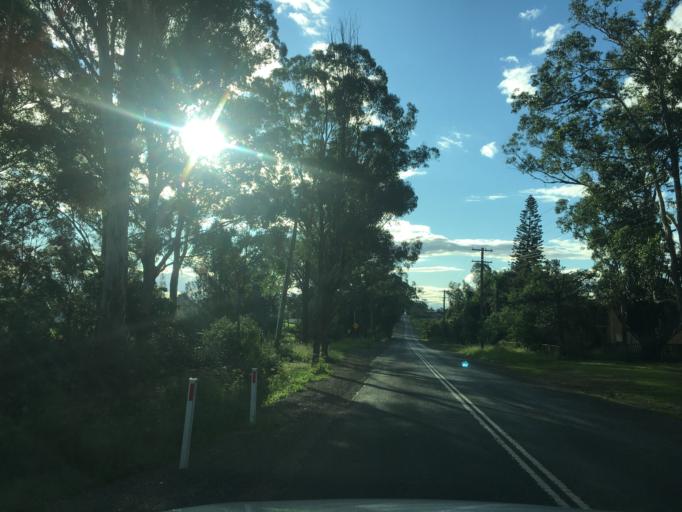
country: AU
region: New South Wales
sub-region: Campbelltown Municipality
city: Denham Court
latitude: -33.9717
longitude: 150.8035
